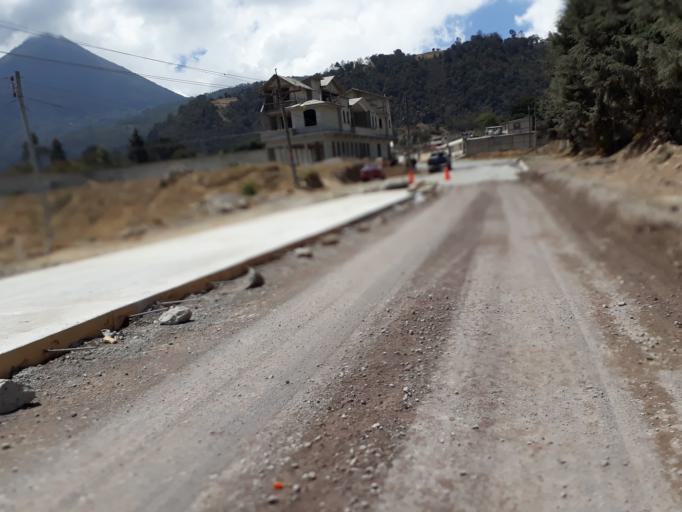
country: GT
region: Quetzaltenango
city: Quetzaltenango
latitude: 14.8091
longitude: -91.5519
